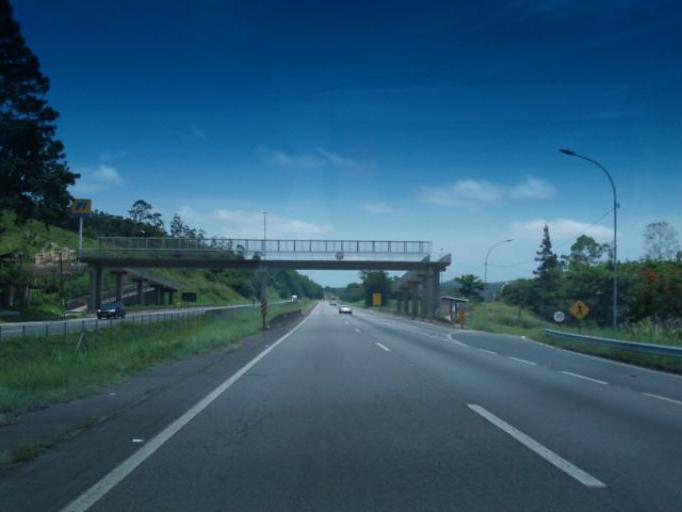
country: BR
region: Sao Paulo
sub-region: Miracatu
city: Miracatu
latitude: -24.2858
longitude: -47.4442
